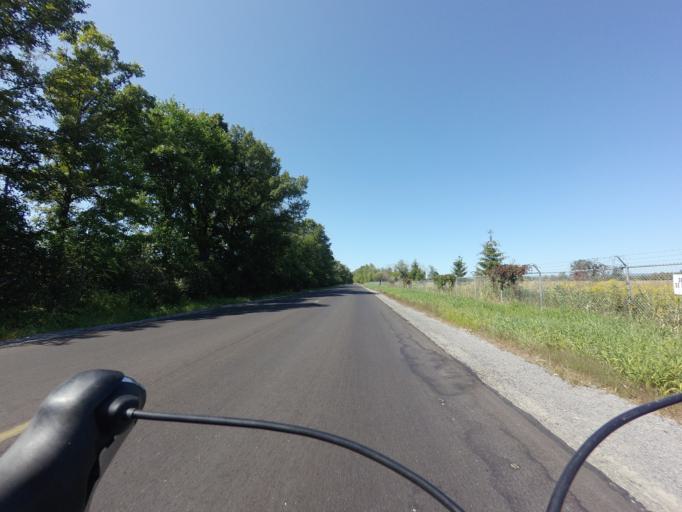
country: CA
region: Ontario
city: Bells Corners
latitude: 45.3690
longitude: -75.9266
